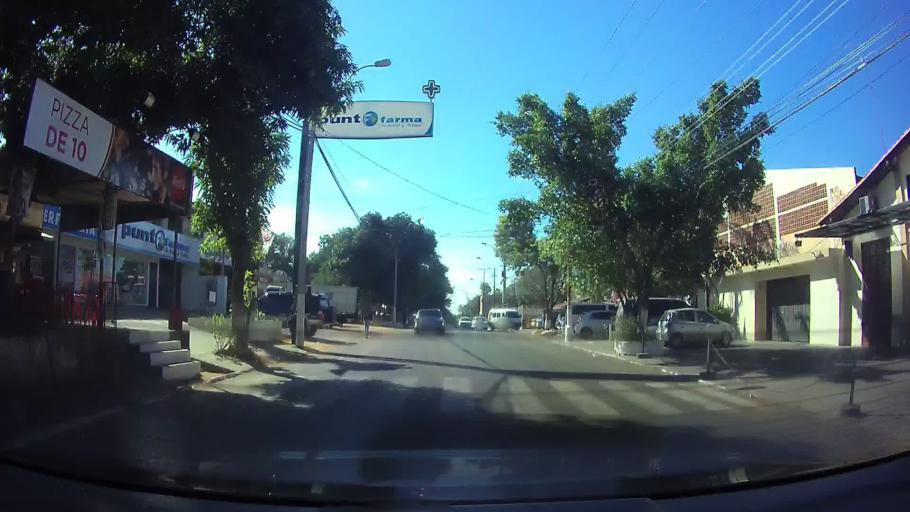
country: PY
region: Central
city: Villa Elisa
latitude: -25.3758
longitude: -57.5819
